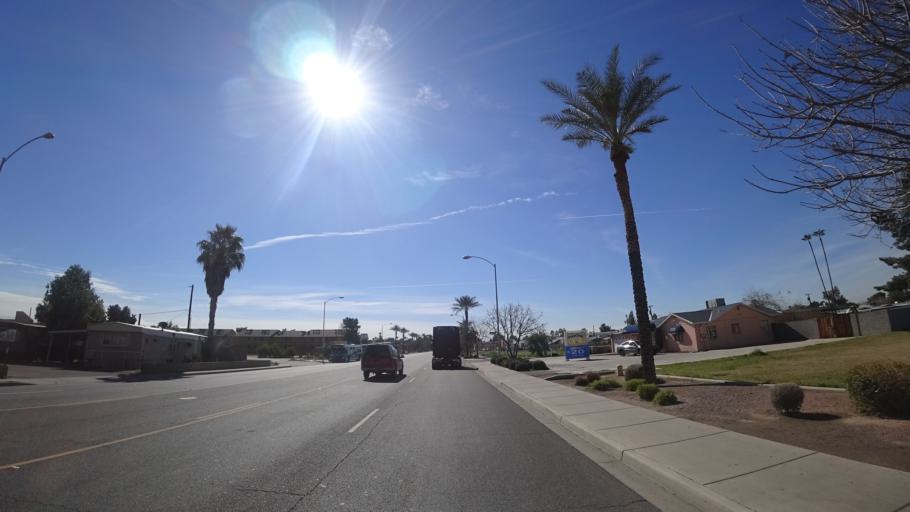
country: US
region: Arizona
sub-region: Maricopa County
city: Glendale
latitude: 33.5287
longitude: -112.1864
